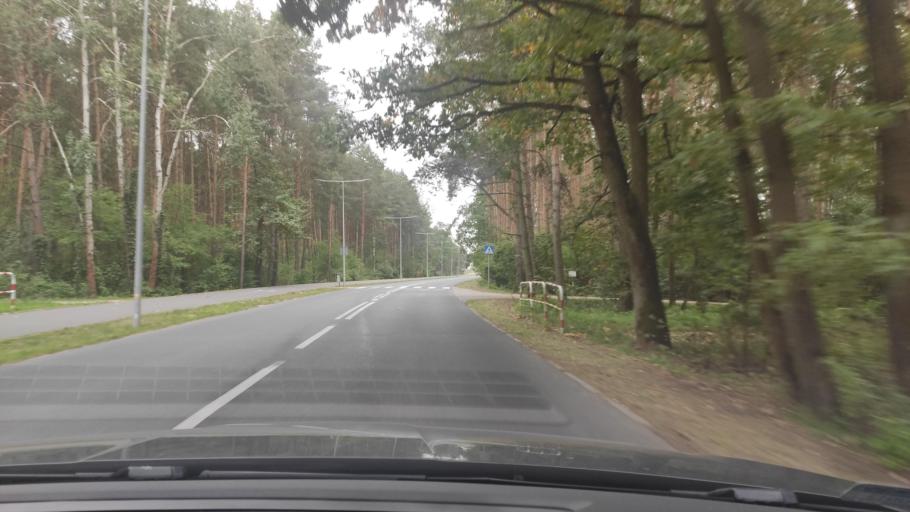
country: PL
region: Greater Poland Voivodeship
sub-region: Powiat poznanski
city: Swarzedz
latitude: 52.3862
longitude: 17.0537
